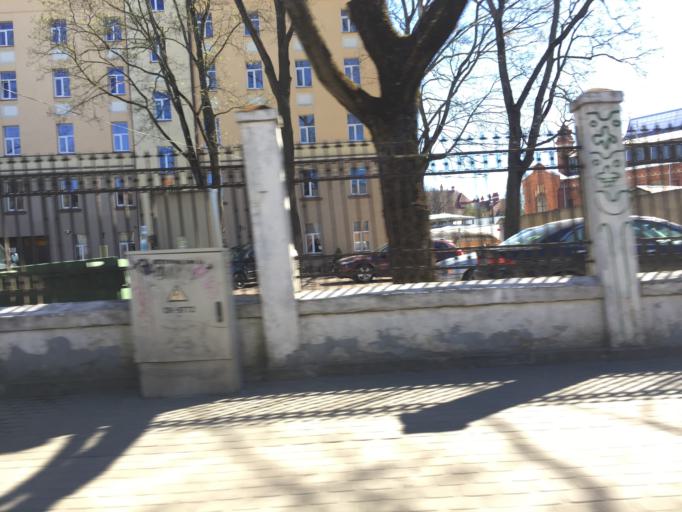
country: LV
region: Riga
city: Riga
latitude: 56.9364
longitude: 24.0711
